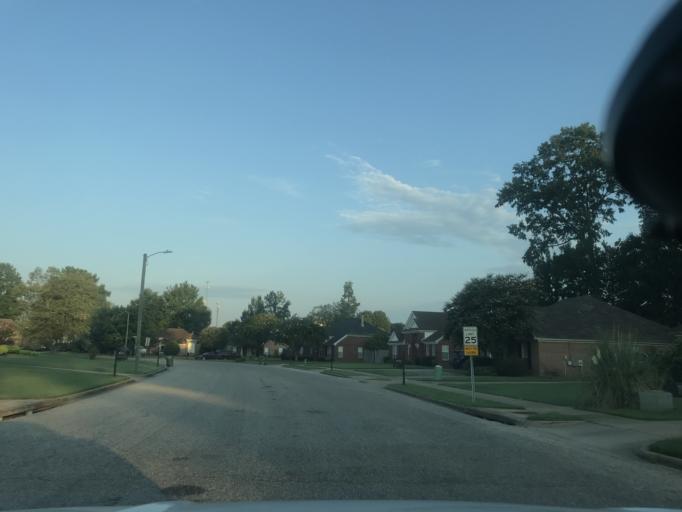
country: US
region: Alabama
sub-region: Montgomery County
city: Pike Road
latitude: 32.3703
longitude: -86.1620
